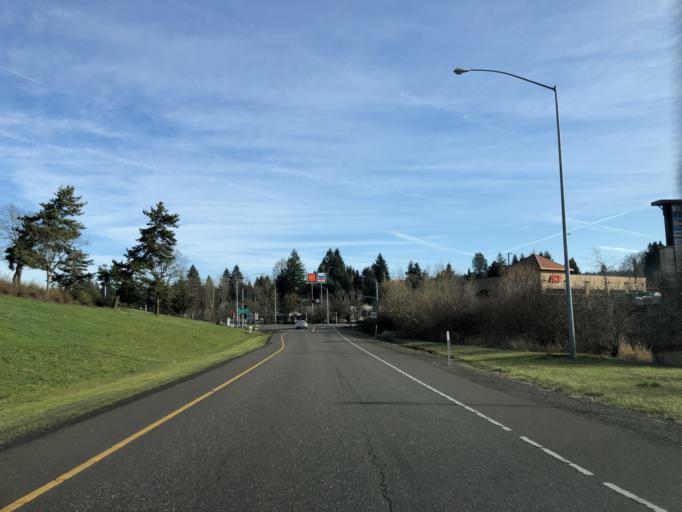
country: US
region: Oregon
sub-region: Clackamas County
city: West Linn
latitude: 45.3472
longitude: -122.6534
